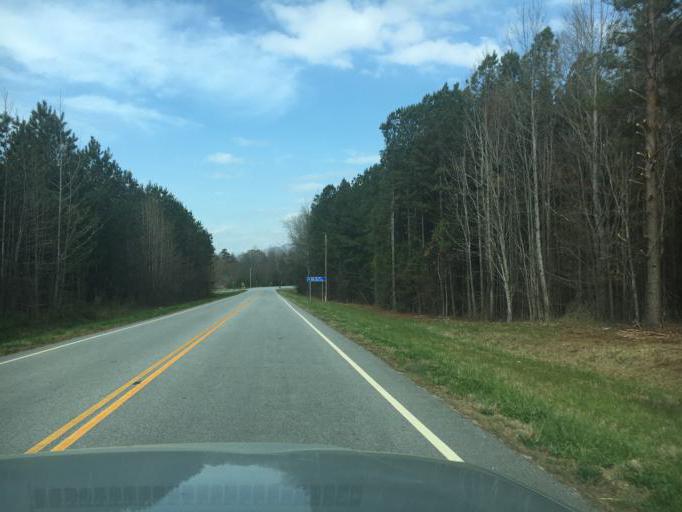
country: US
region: South Carolina
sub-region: Spartanburg County
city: Landrum
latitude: 35.1157
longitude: -82.2423
